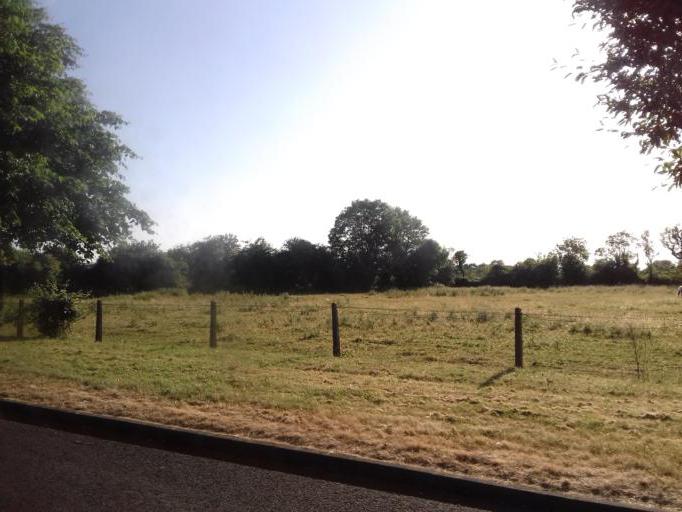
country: IE
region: Leinster
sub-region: Fingal County
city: Swords
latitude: 53.4935
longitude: -6.2981
